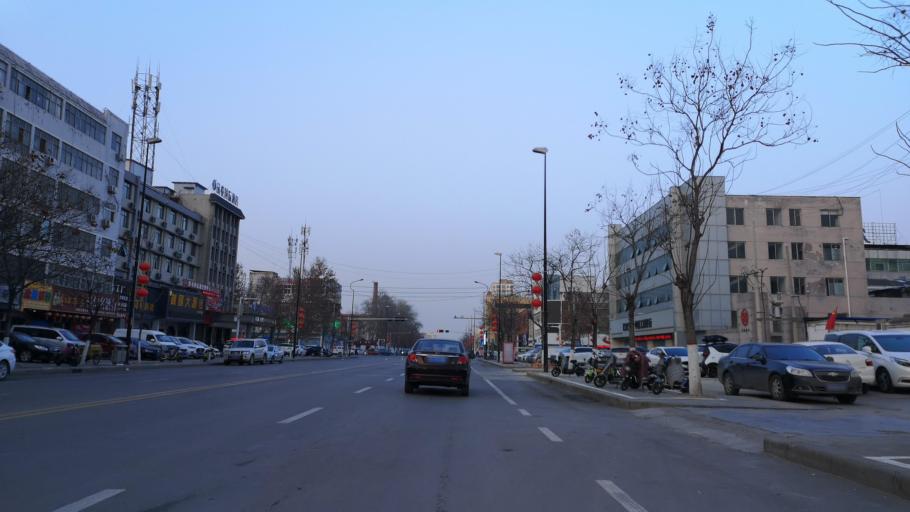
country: CN
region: Henan Sheng
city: Zhongyuanlu
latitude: 35.7769
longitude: 115.0603
